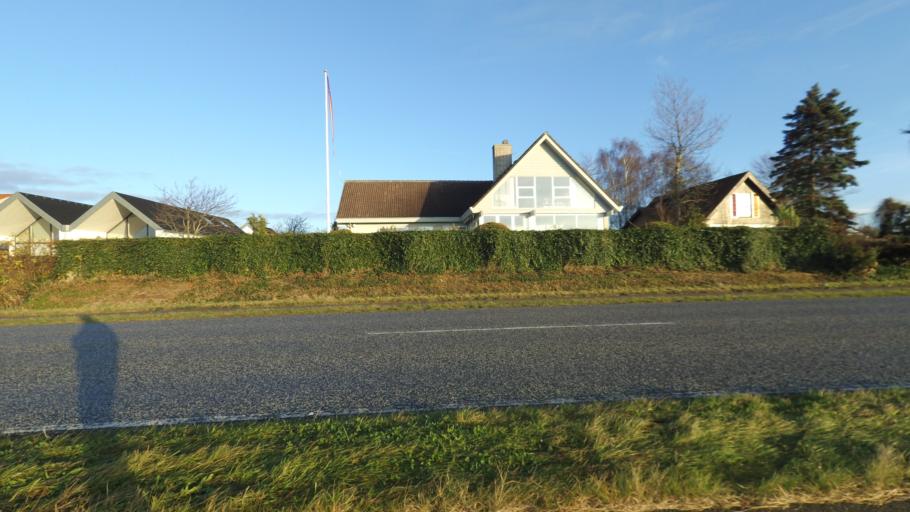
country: DK
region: Central Jutland
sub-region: Arhus Kommune
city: Beder
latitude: 56.0196
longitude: 10.2615
